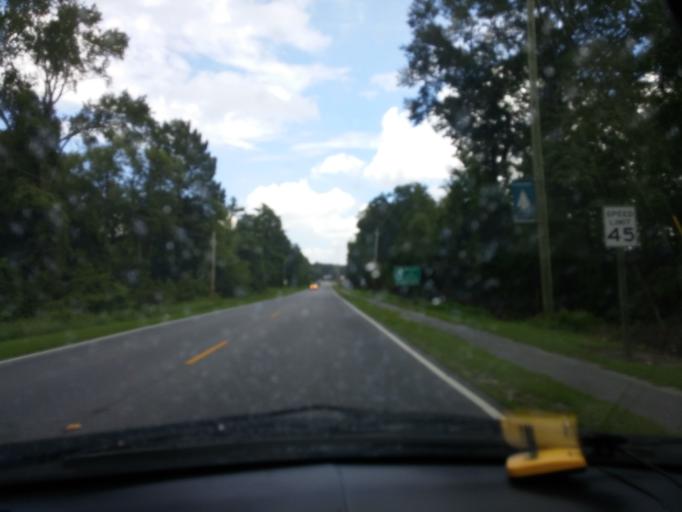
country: US
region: North Carolina
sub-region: Pitt County
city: Grifton
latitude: 35.3708
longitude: -77.4447
